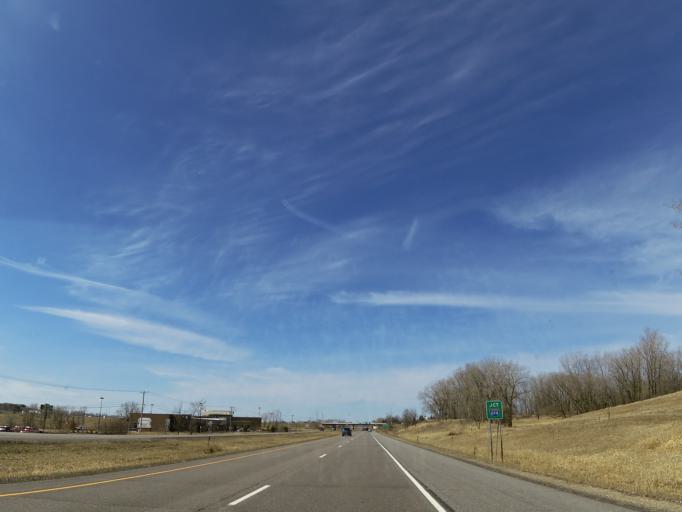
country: US
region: Minnesota
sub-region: Washington County
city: Oakdale
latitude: 44.9979
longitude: -92.9525
